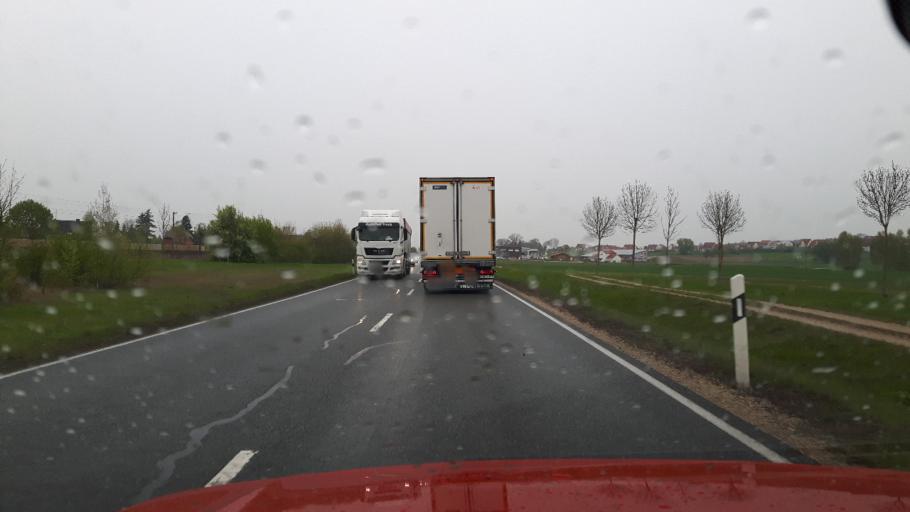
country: DE
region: Bavaria
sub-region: Regierungsbezirk Mittelfranken
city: Muhr am See
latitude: 49.1504
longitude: 10.7305
